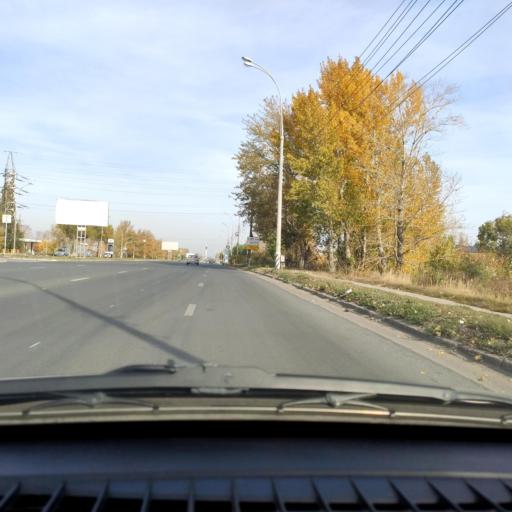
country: RU
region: Samara
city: Tol'yatti
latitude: 53.5443
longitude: 49.2857
